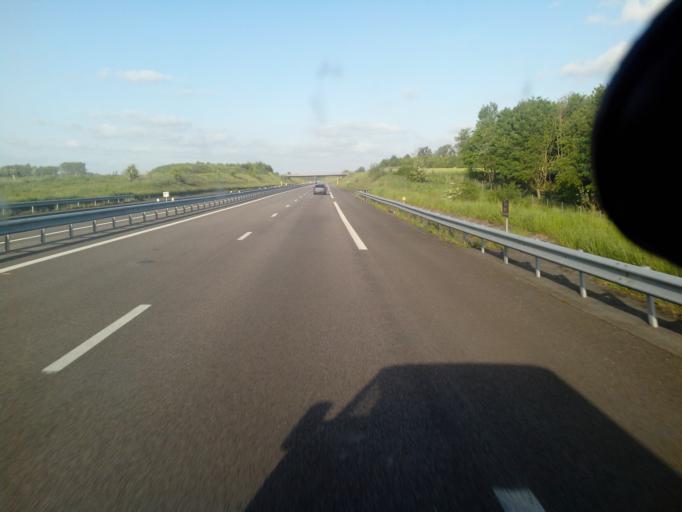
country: FR
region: Haute-Normandie
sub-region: Departement de la Seine-Maritime
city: Bosc-le-Hard
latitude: 49.6361
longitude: 1.1663
